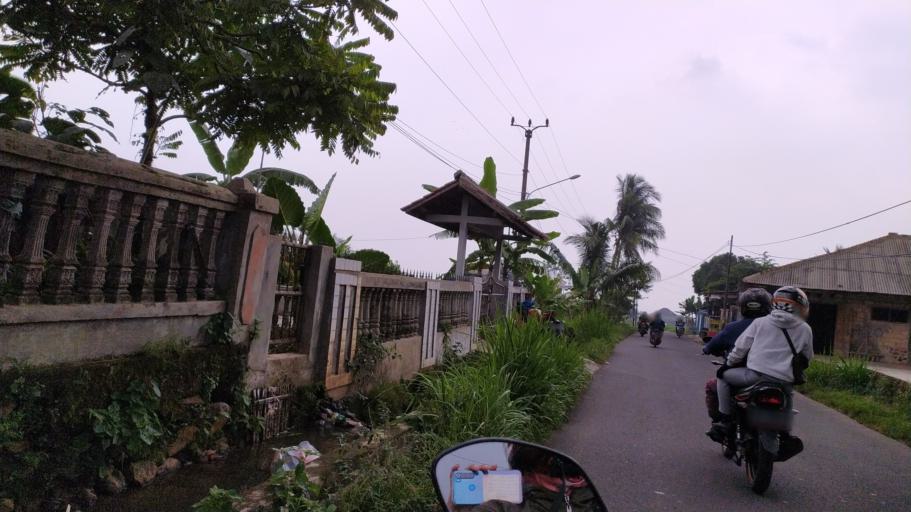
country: ID
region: West Java
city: Ciampea
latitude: -6.6117
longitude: 106.6980
